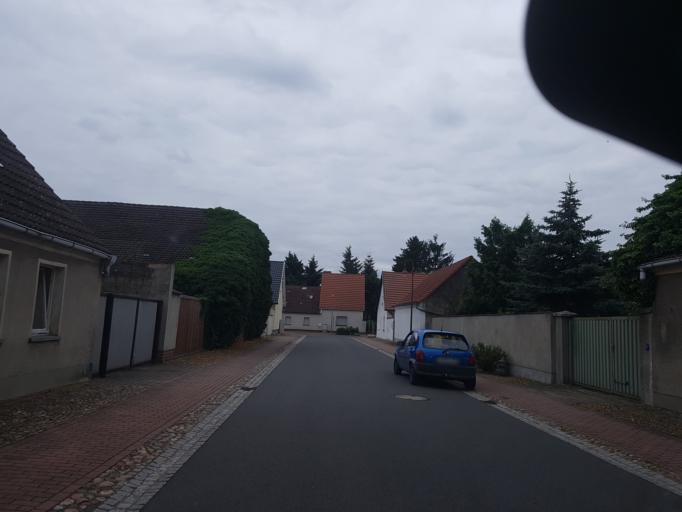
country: DE
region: Saxony-Anhalt
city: Seyda
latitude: 51.8806
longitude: 12.9066
